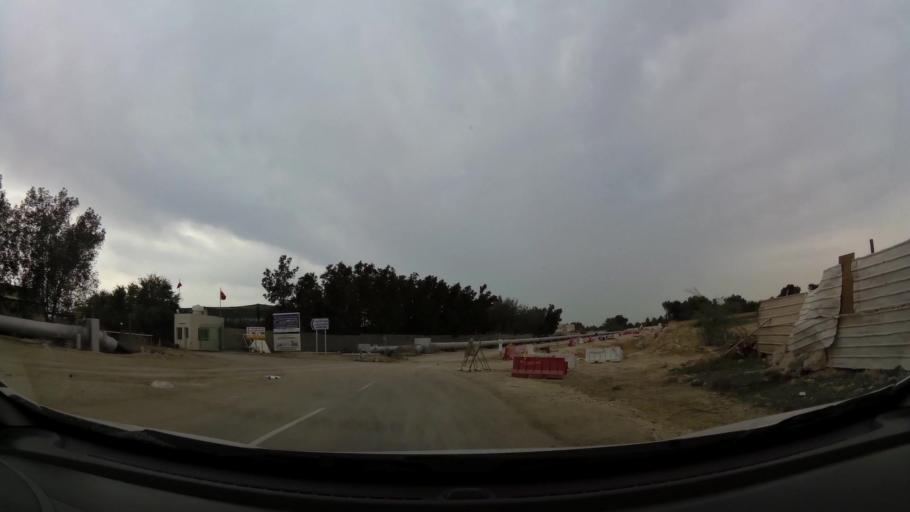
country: BH
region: Central Governorate
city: Madinat Hamad
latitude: 26.1439
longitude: 50.4735
